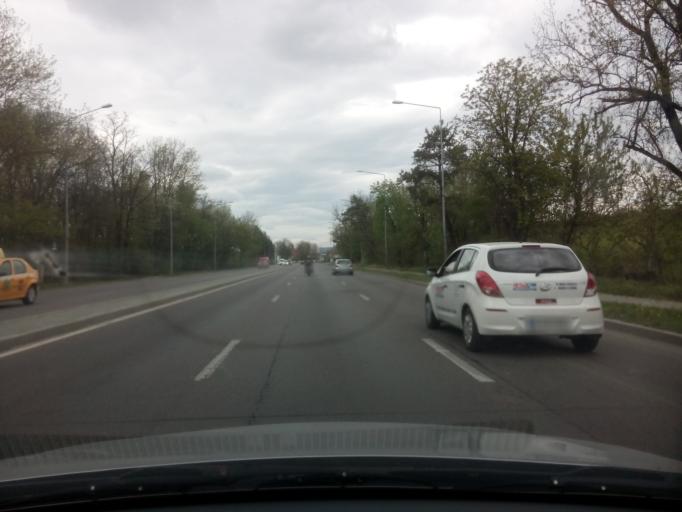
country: RO
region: Ilfov
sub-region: Comuna Otopeni
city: Otopeni
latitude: 44.5224
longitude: 26.0744
